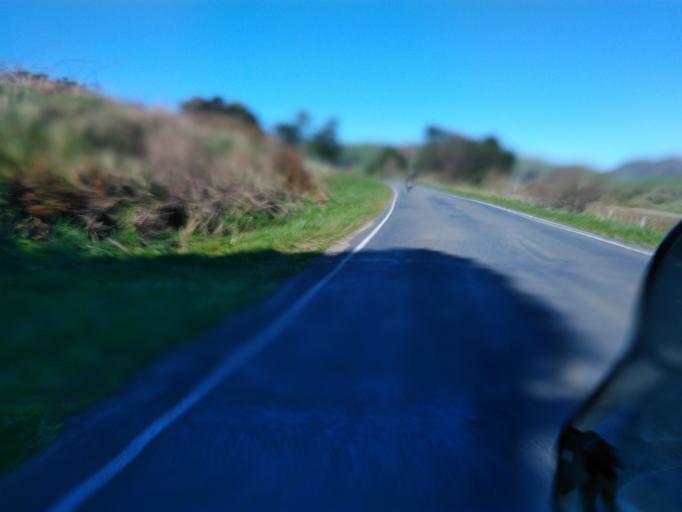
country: NZ
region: Bay of Plenty
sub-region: Opotiki District
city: Opotiki
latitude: -38.3448
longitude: 177.5331
